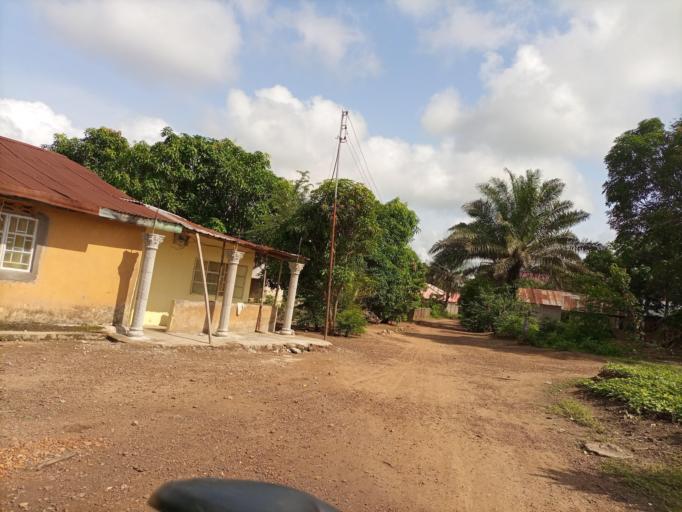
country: SL
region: Southern Province
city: Bo
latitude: 7.9678
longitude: -11.7632
